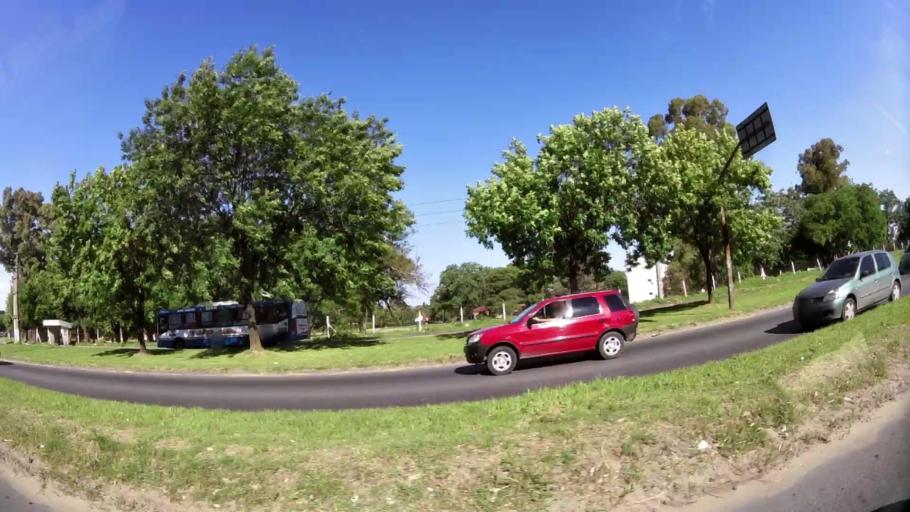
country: AR
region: Buenos Aires
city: Caseros
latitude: -34.5642
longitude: -58.5888
